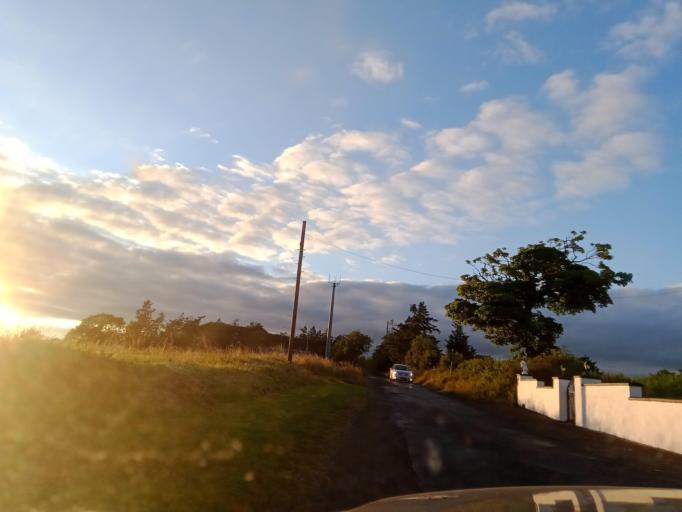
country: IE
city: Ballylinan
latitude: 52.8973
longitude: -7.1311
